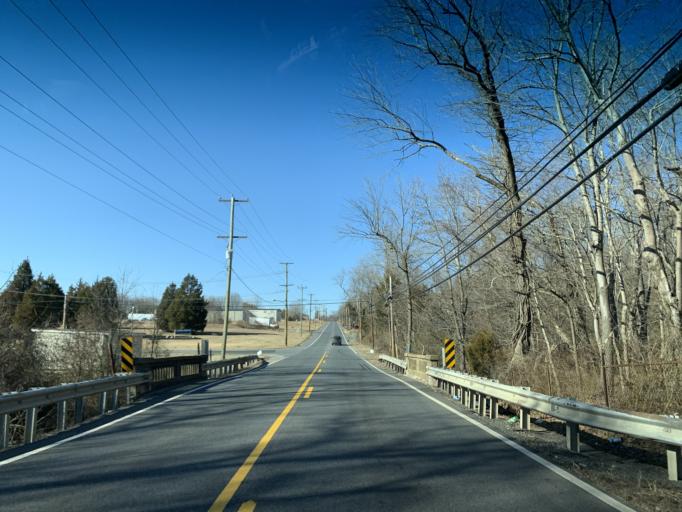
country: US
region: Maryland
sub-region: Cecil County
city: Elkton
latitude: 39.6161
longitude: -75.8489
